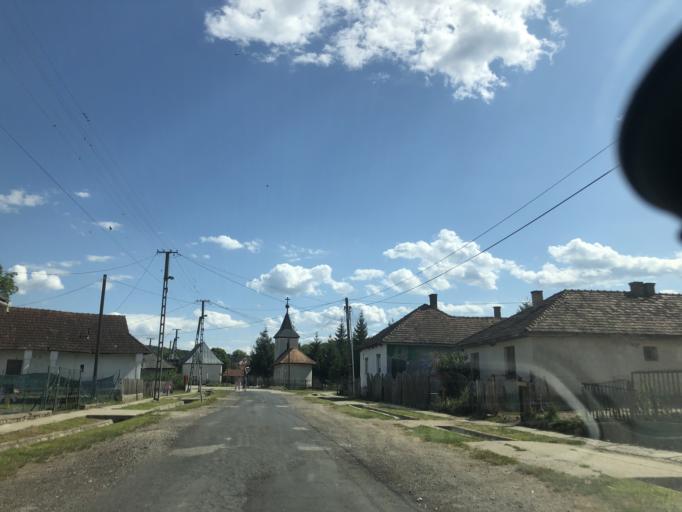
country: HU
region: Borsod-Abauj-Zemplen
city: Szendro
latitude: 48.5434
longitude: 20.8034
